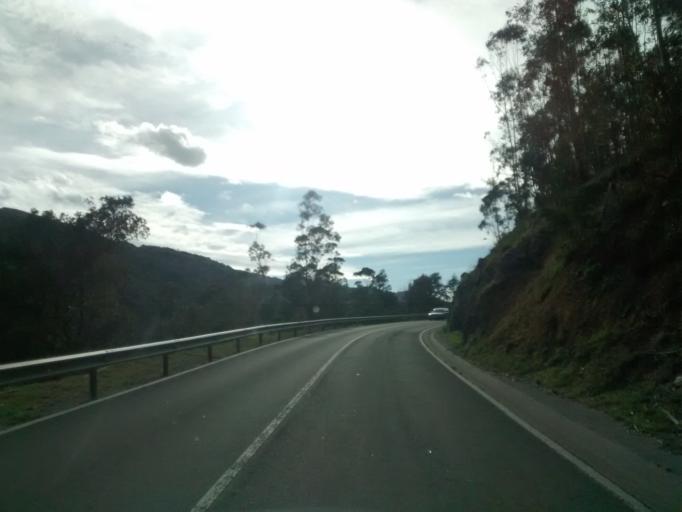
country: ES
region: Cantabria
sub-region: Provincia de Cantabria
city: Arredondo
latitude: 43.2799
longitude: -3.6142
